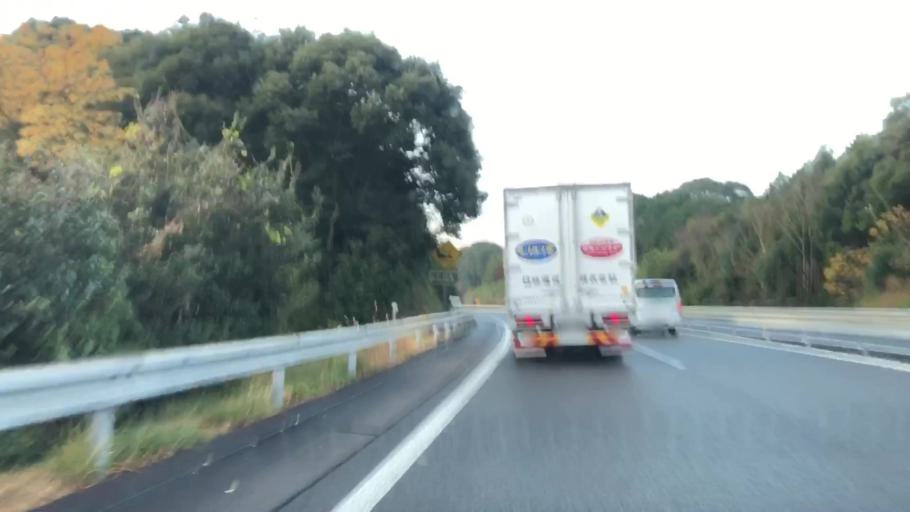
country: JP
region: Nagasaki
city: Sasebo
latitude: 33.1584
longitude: 129.8145
